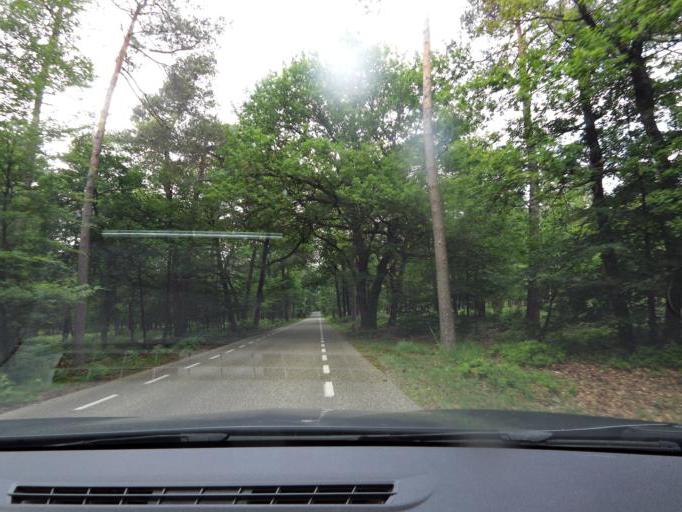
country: NL
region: Gelderland
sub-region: Gemeente Apeldoorn
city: Uddel
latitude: 52.2378
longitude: 5.8295
